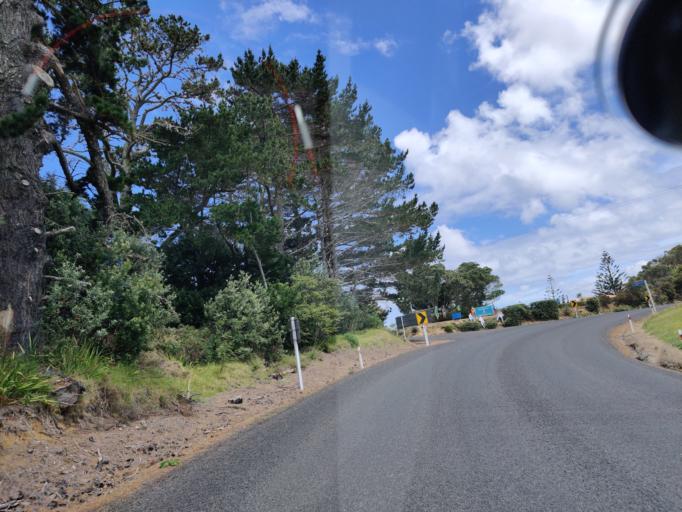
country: NZ
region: Northland
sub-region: Far North District
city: Kaitaia
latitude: -34.9357
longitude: 173.1869
